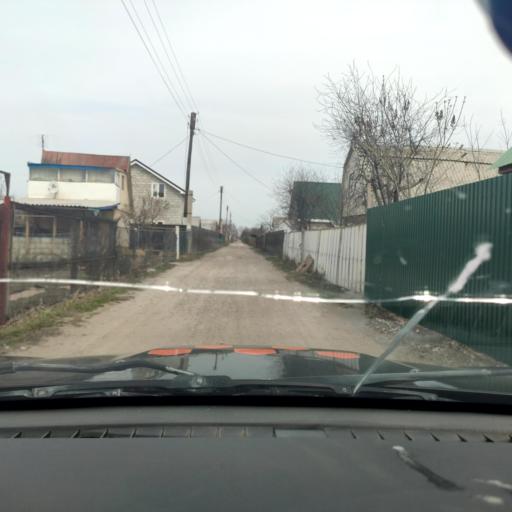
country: RU
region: Samara
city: Tol'yatti
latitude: 53.5984
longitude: 49.2452
